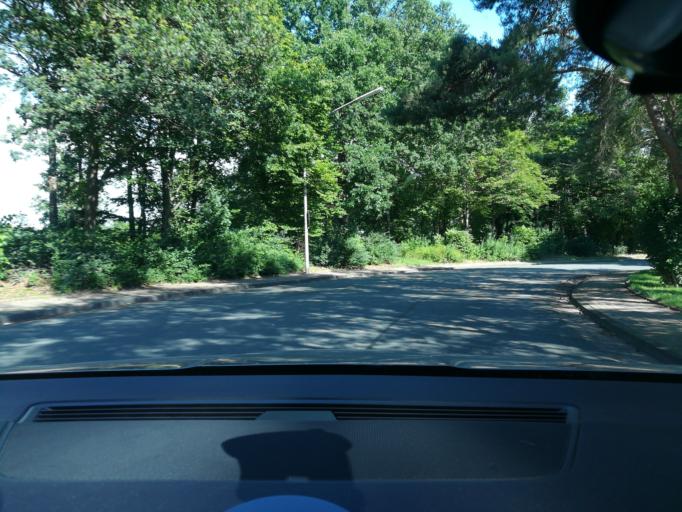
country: DE
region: North Rhine-Westphalia
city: Lubbecke
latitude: 52.3296
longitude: 8.6233
